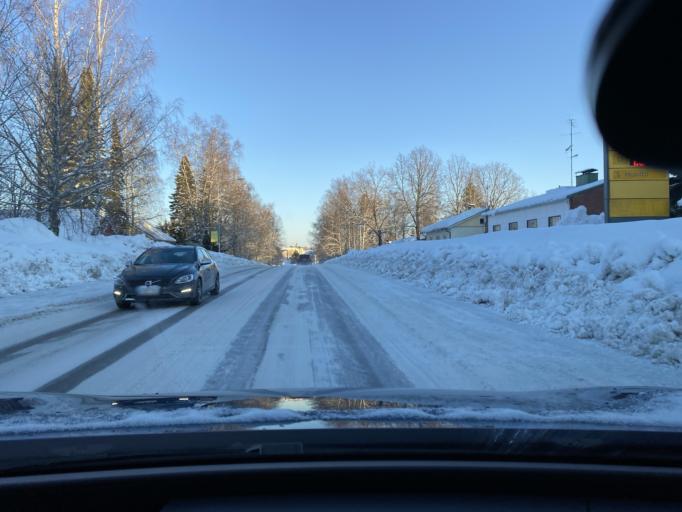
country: FI
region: Southern Savonia
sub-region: Mikkeli
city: Kangasniemi
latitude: 61.9907
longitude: 26.6354
